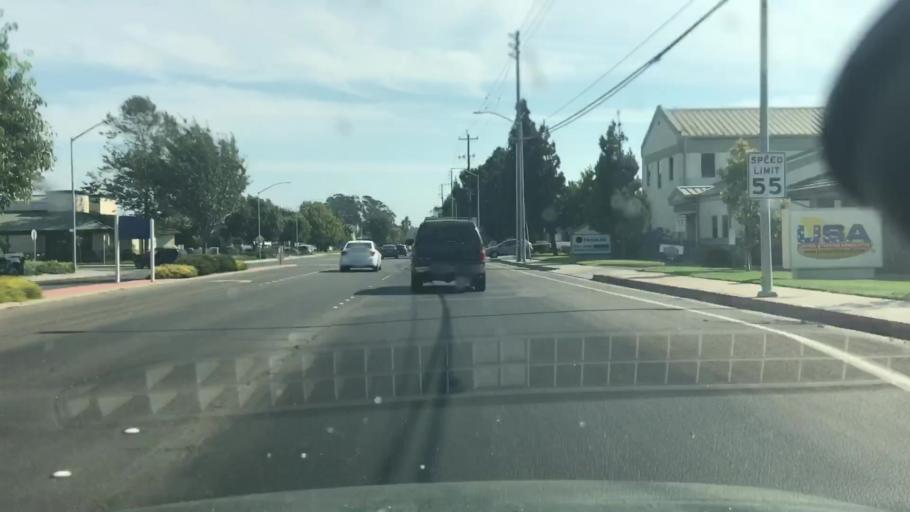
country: US
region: California
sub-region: Santa Barbara County
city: Santa Maria
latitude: 34.9203
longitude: -120.4541
